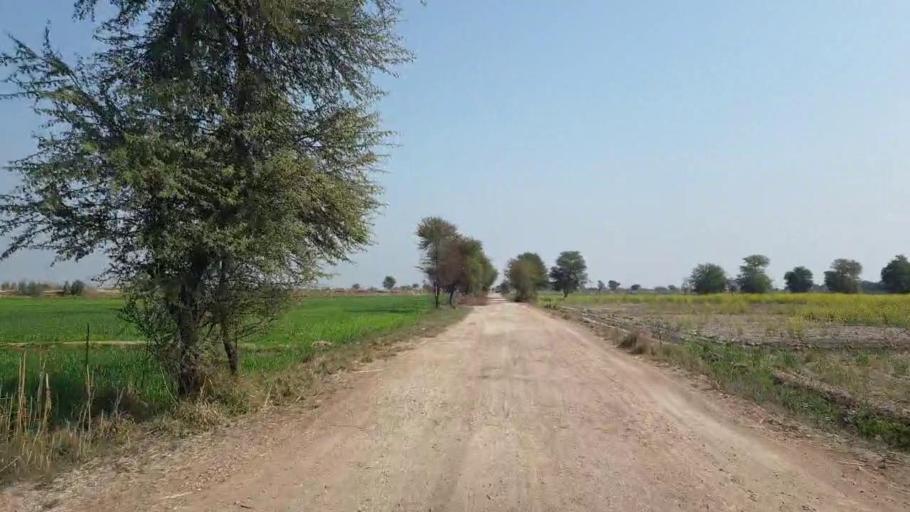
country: PK
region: Sindh
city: Shahdadpur
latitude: 25.9453
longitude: 68.4822
